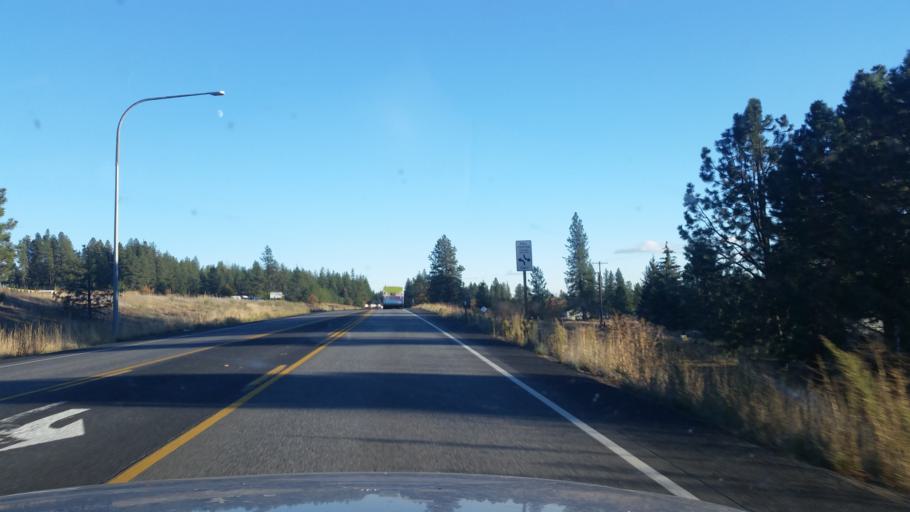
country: US
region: Washington
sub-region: Spokane County
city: Cheney
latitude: 47.5438
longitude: -117.5833
